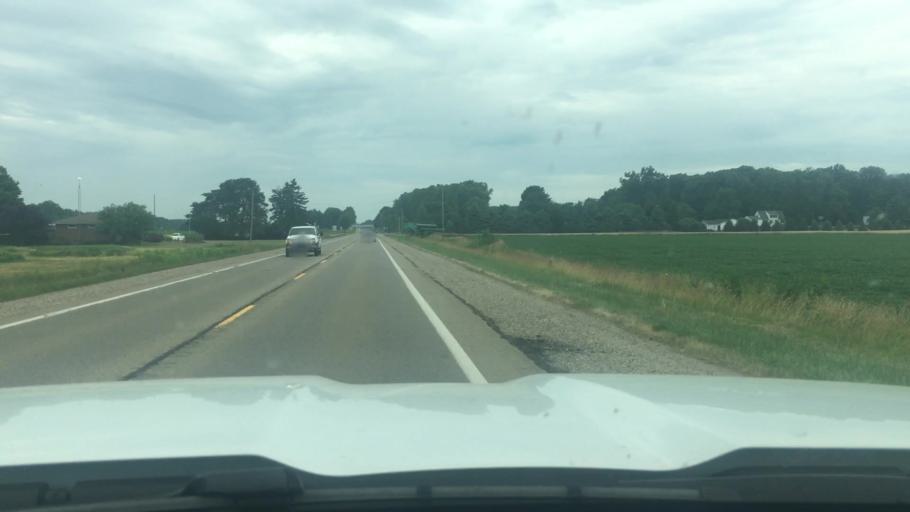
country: US
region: Michigan
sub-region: Clinton County
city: Saint Johns
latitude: 43.0013
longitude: -84.4987
